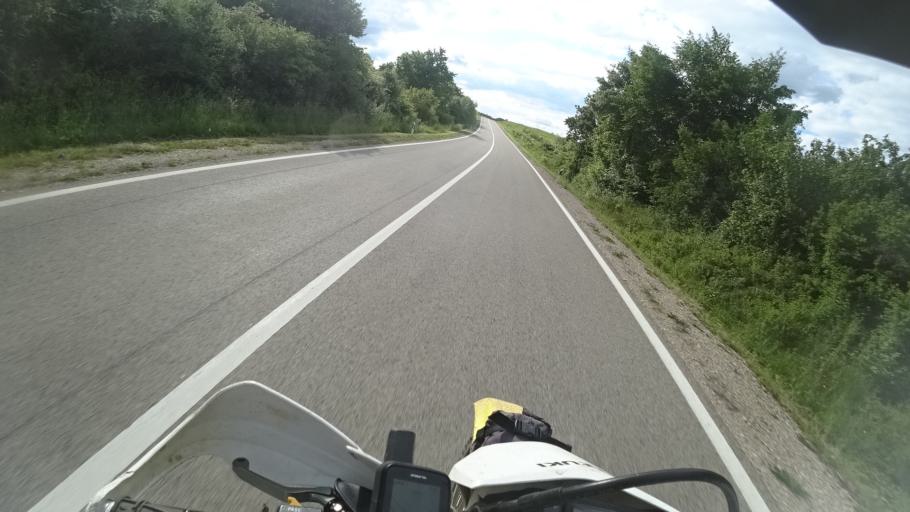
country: HR
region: Licko-Senjska
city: Gospic
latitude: 44.5018
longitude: 15.4510
